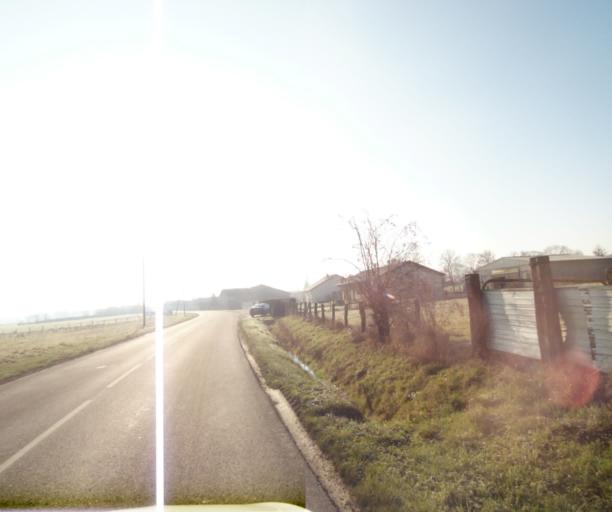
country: FR
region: Champagne-Ardenne
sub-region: Departement de la Haute-Marne
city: Montier-en-Der
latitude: 48.4623
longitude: 4.7663
